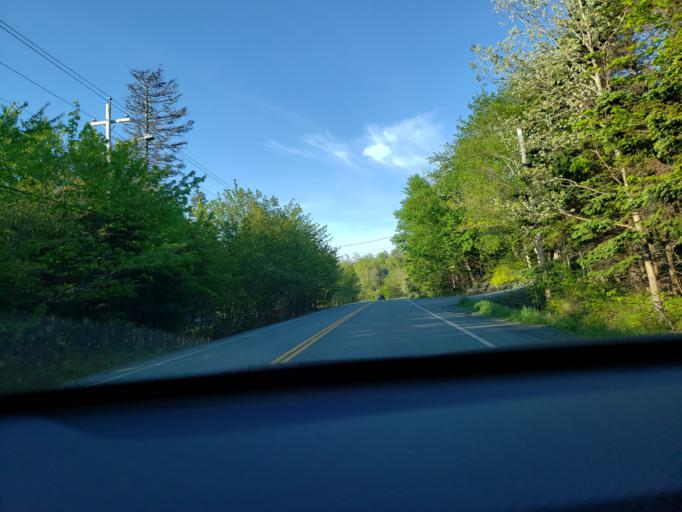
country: CA
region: Nova Scotia
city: Cole Harbour
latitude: 44.7292
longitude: -63.3942
